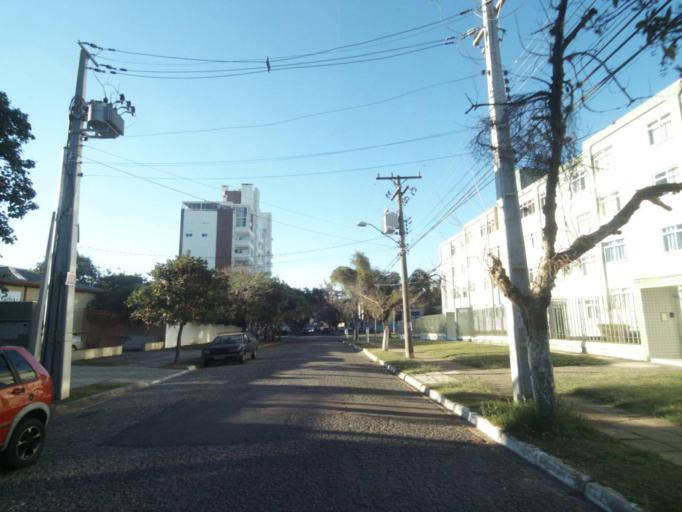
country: BR
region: Parana
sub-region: Curitiba
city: Curitiba
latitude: -25.4608
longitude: -49.2953
